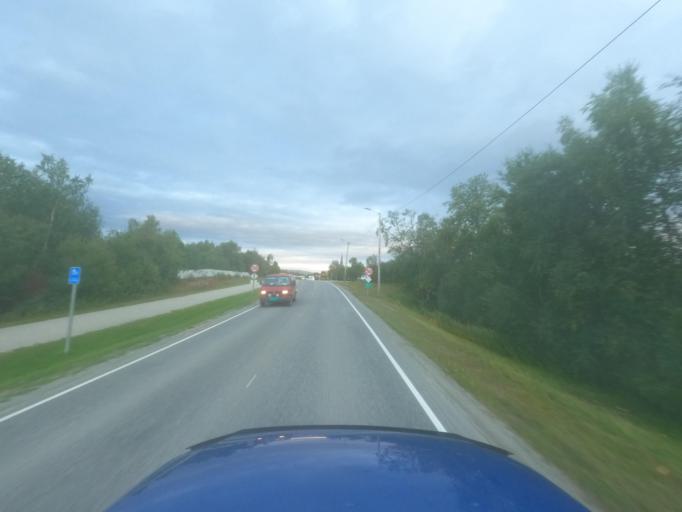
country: NO
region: Finnmark Fylke
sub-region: Porsanger
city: Lakselv
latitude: 70.0514
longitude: 24.9469
